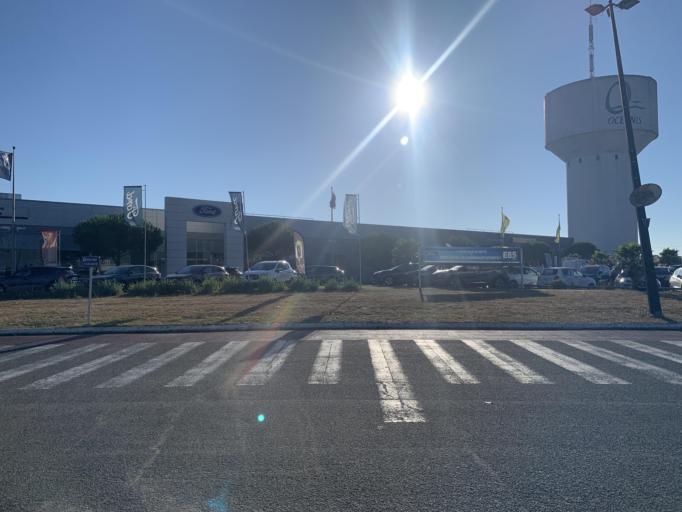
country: FR
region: Pays de la Loire
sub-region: Departement de la Loire-Atlantique
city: Pornichet
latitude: 47.2569
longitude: -2.2698
